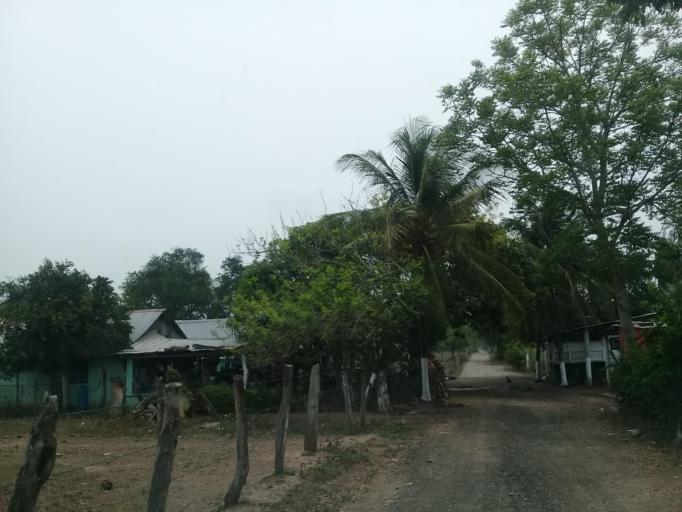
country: MX
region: Veracruz
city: Jamapa
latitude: 18.9556
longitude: -96.2055
